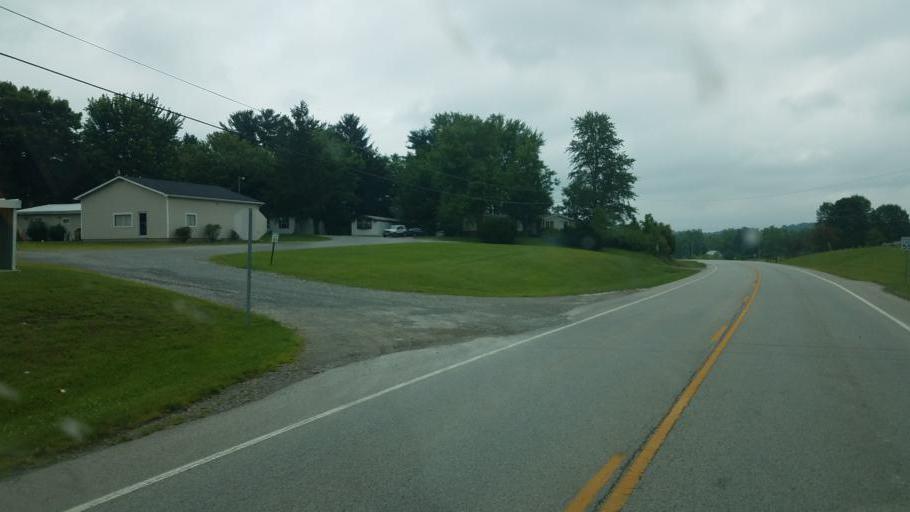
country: US
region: Ohio
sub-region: Highland County
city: Hillsboro
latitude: 39.2108
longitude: -83.5574
